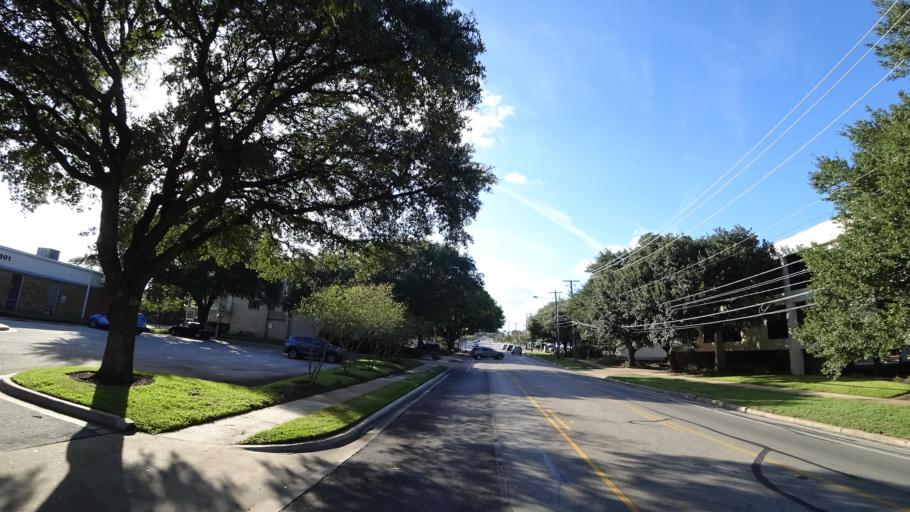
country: US
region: Texas
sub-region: Williamson County
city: Jollyville
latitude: 30.3659
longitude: -97.7377
